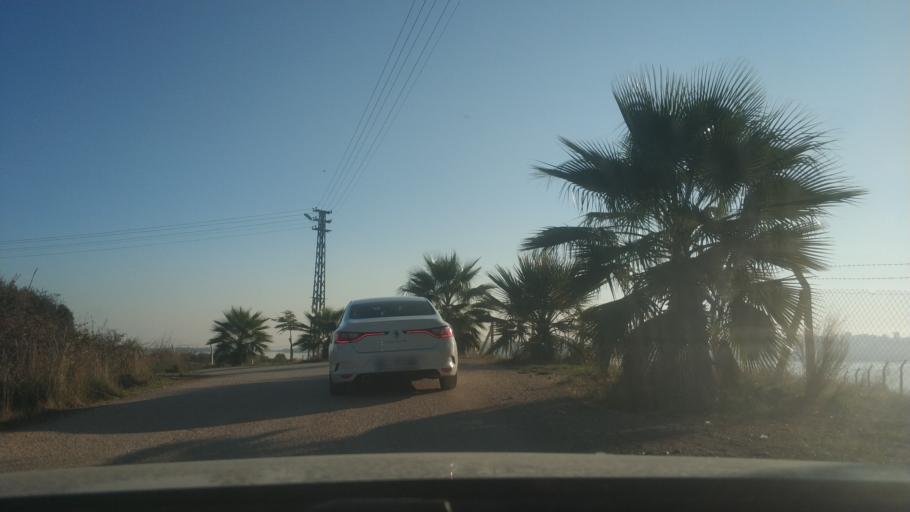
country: TR
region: Adana
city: Adana
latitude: 37.0914
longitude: 35.3056
